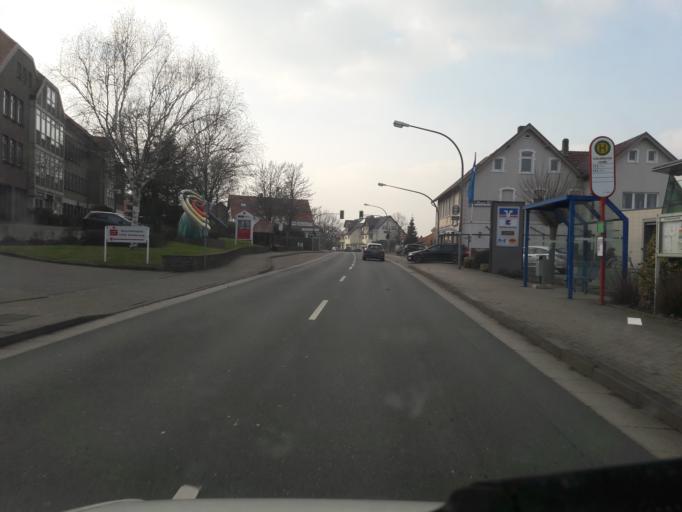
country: DE
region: North Rhine-Westphalia
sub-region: Regierungsbezirk Detmold
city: Huellhorst
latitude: 52.3015
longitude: 8.6988
